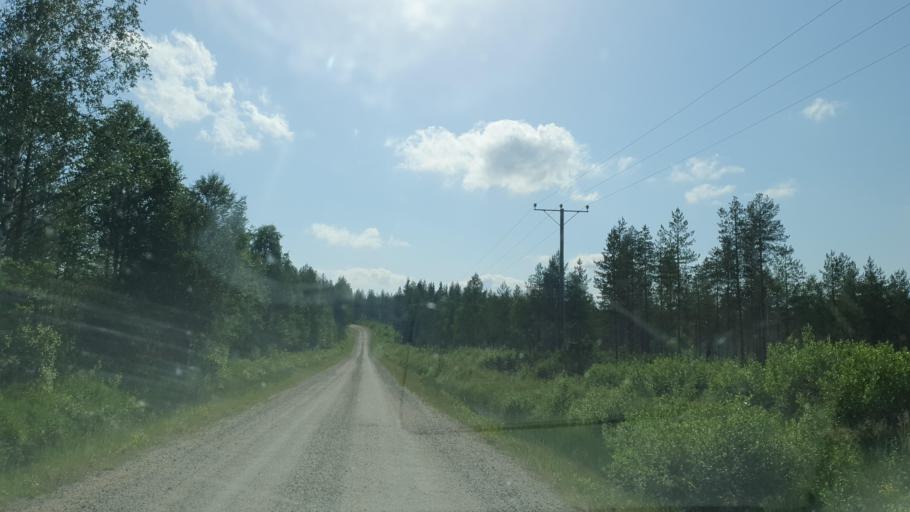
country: FI
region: Kainuu
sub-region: Kehys-Kainuu
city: Kuhmo
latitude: 64.0355
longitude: 29.9373
